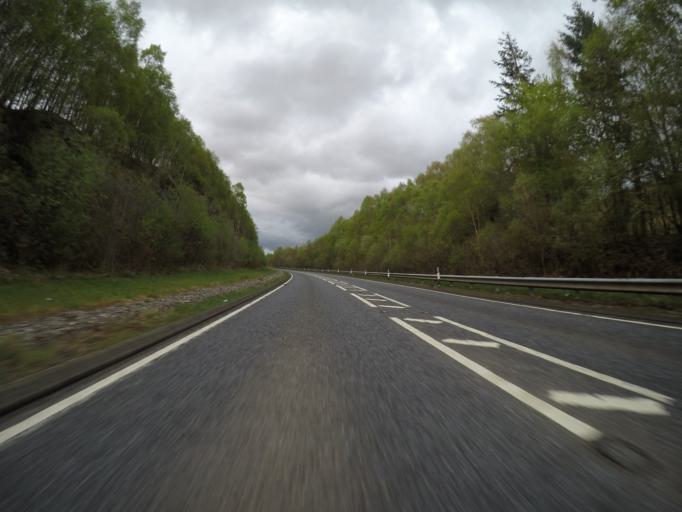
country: GB
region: Scotland
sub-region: Argyll and Bute
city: Garelochhead
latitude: 56.3507
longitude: -4.6917
